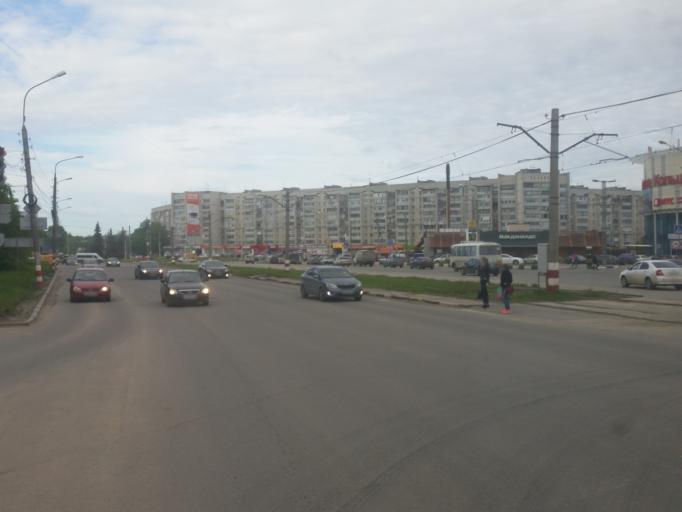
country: RU
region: Ulyanovsk
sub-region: Ulyanovskiy Rayon
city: Ulyanovsk
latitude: 54.3043
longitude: 48.3489
